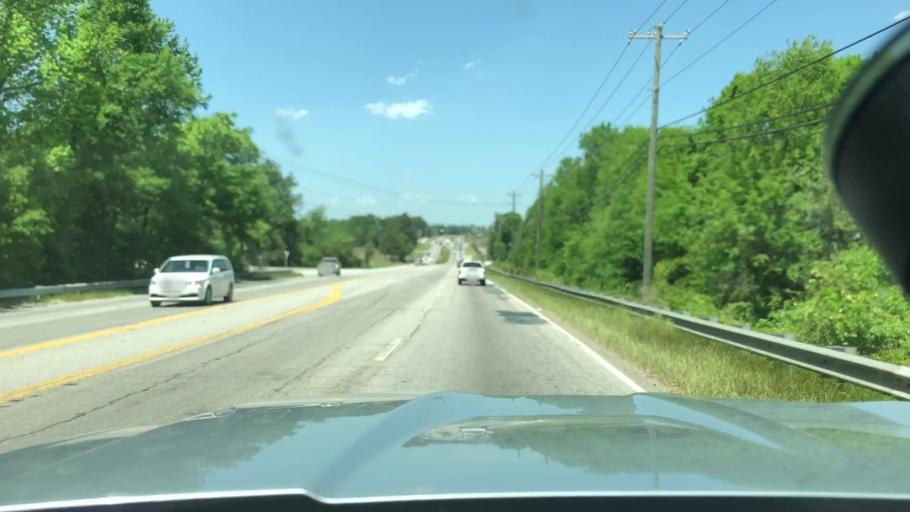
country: US
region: South Carolina
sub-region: Lexington County
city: Pineridge
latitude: 33.9095
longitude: -81.0673
